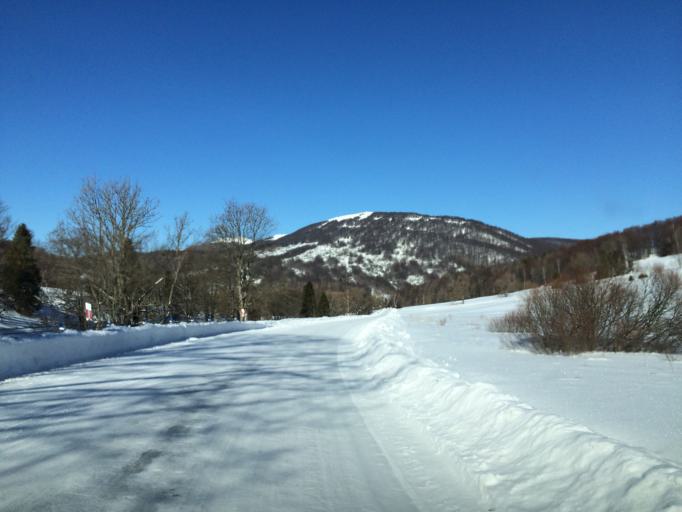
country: PL
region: Subcarpathian Voivodeship
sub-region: Powiat bieszczadzki
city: Lutowiska
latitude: 49.1317
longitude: 22.5768
